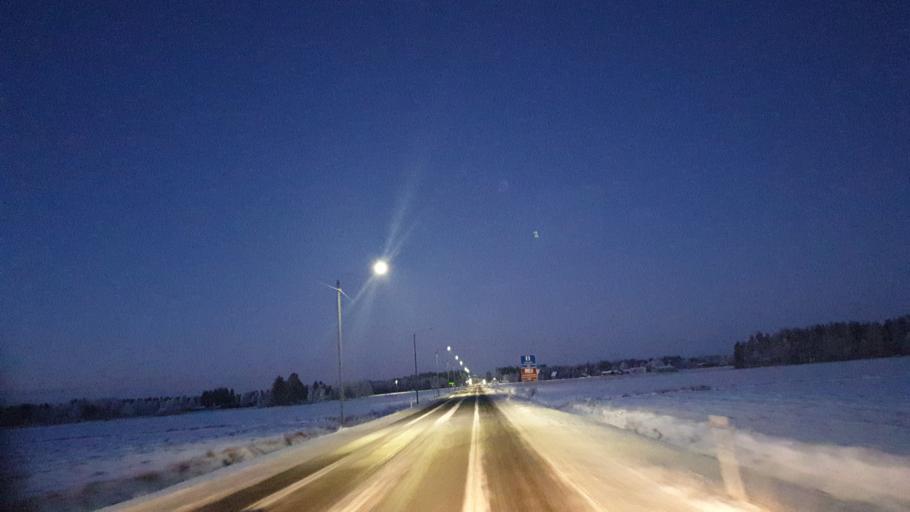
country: FI
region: Northern Ostrobothnia
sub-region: Raahe
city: Ruukki
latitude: 64.7223
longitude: 24.9969
